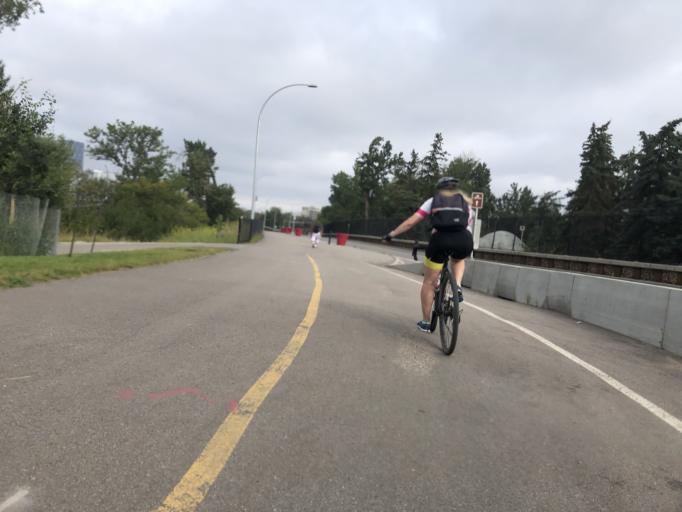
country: CA
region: Alberta
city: Calgary
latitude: 51.0447
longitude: -114.0325
